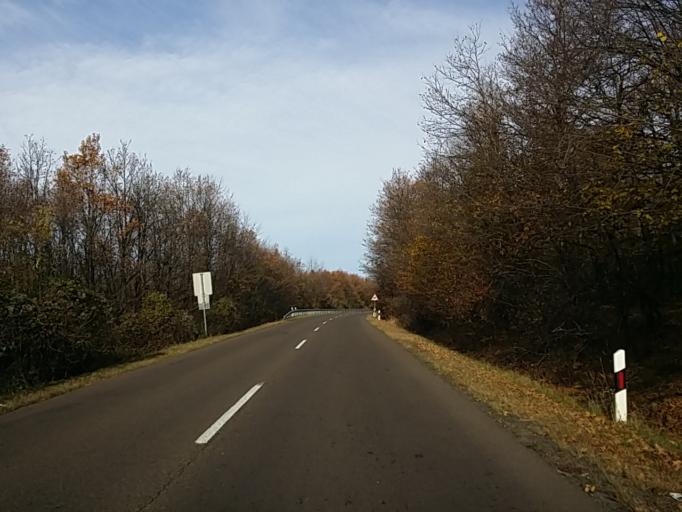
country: HU
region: Heves
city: Gyongyossolymos
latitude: 47.8559
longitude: 19.9693
